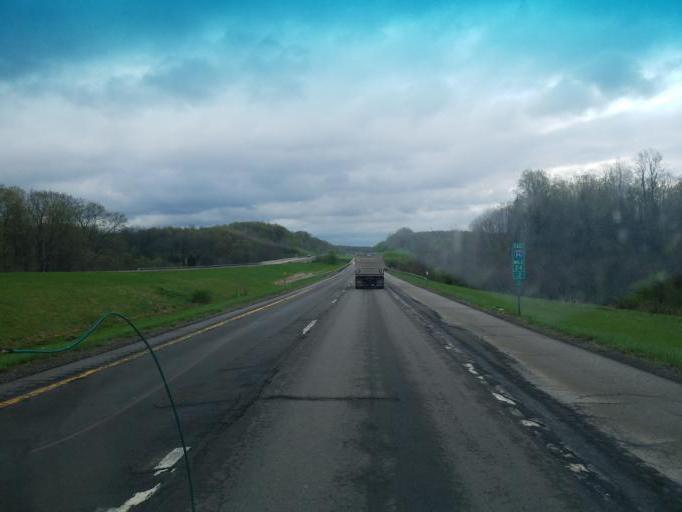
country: US
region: New York
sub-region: Chautauqua County
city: Lakewood
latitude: 42.1280
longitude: -79.3141
